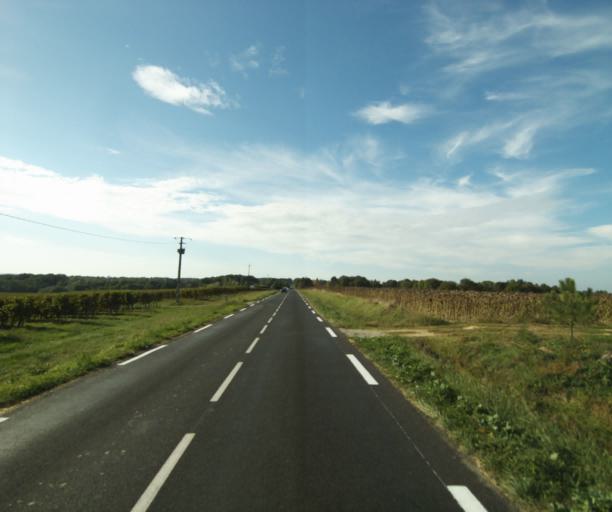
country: FR
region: Midi-Pyrenees
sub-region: Departement du Gers
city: Eauze
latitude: 43.8654
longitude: 0.0554
